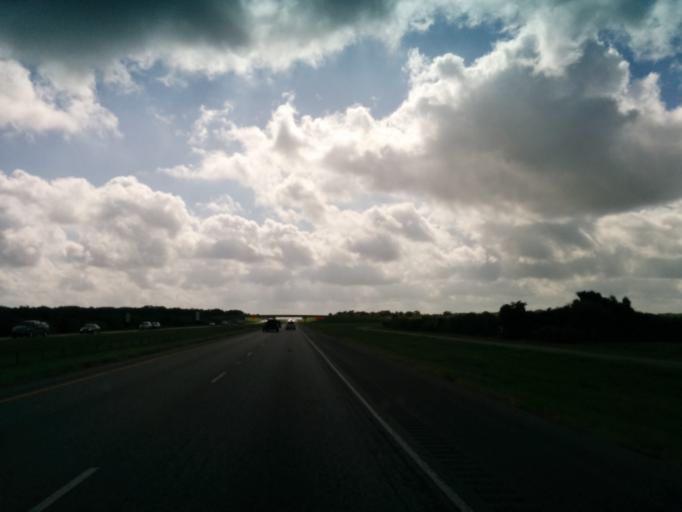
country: US
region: Texas
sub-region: Gonzales County
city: Waelder
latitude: 29.6636
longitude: -97.3690
